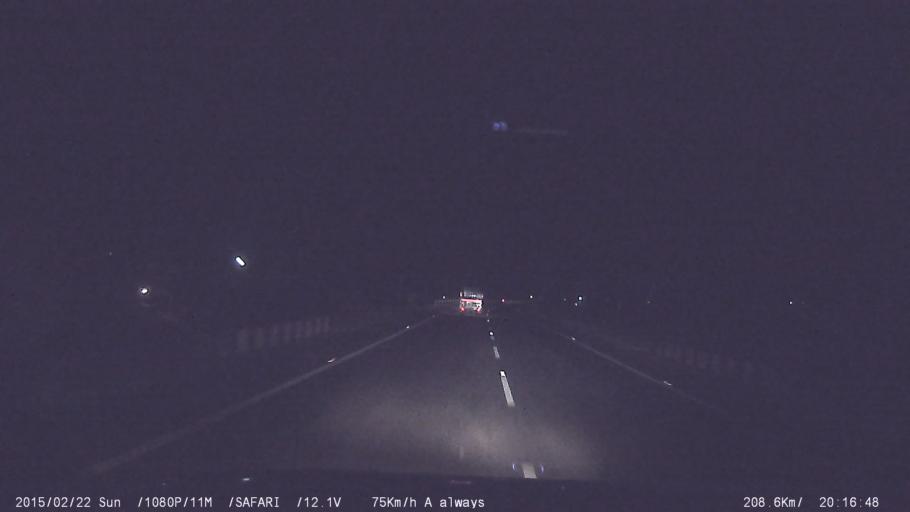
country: IN
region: Tamil Nadu
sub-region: Dindigul
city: Nilakottai
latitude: 10.2662
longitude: 77.8542
